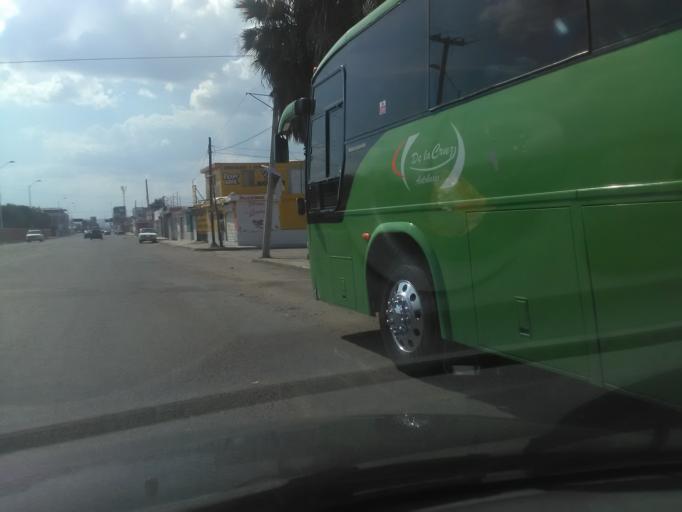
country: MX
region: Durango
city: Victoria de Durango
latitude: 24.0078
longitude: -104.6415
